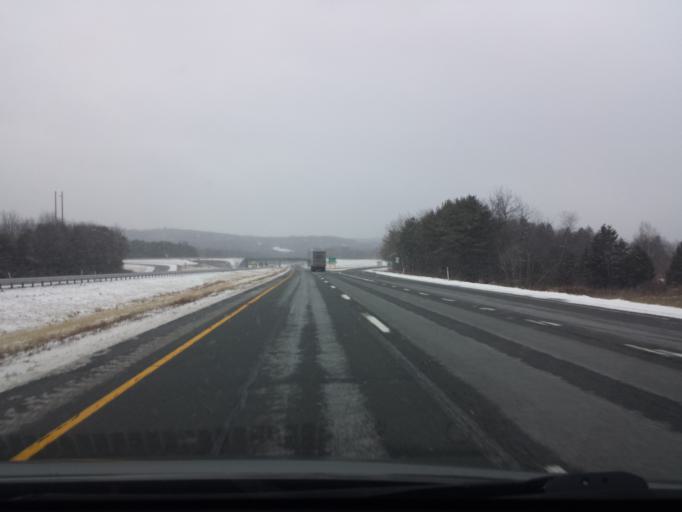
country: US
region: Pennsylvania
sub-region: Carbon County
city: Towamensing Trails
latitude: 41.0768
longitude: -75.5717
